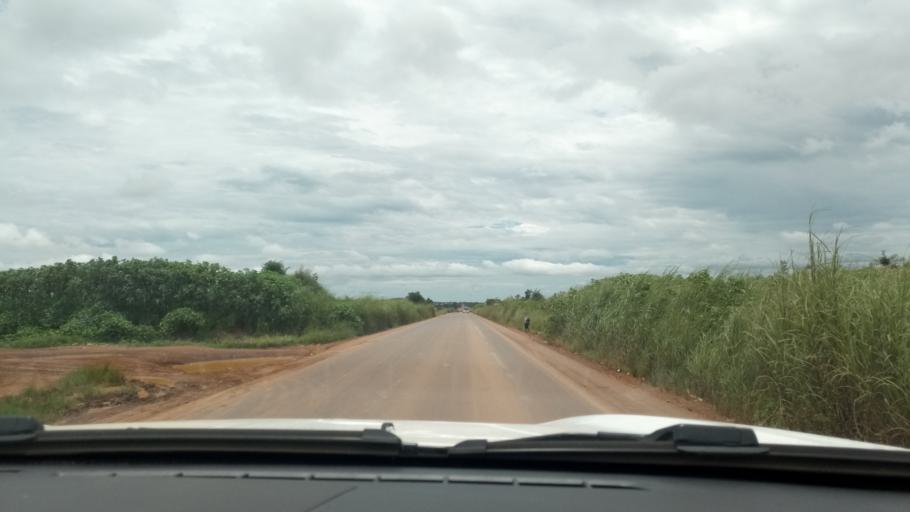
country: CD
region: Katanga
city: Lubumbashi
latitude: -11.5724
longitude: 27.5421
